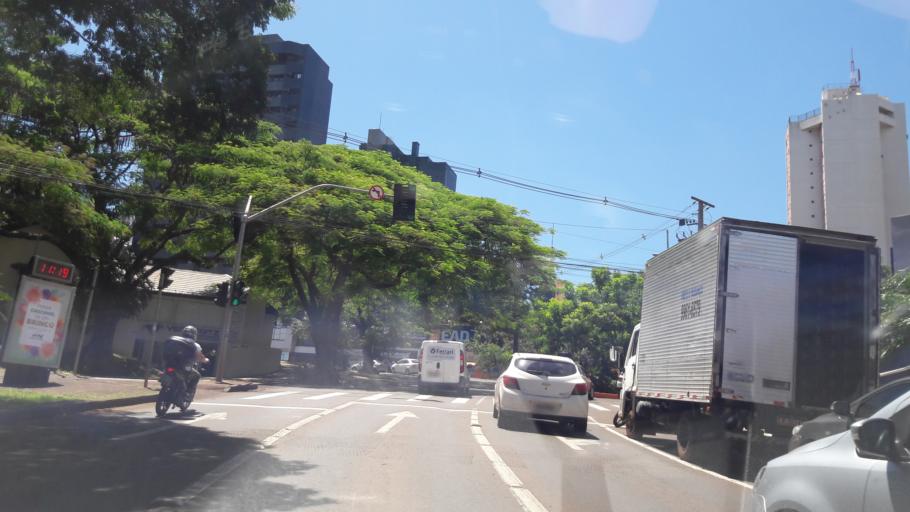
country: BR
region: Parana
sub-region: Cascavel
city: Cascavel
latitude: -24.9523
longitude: -53.4578
